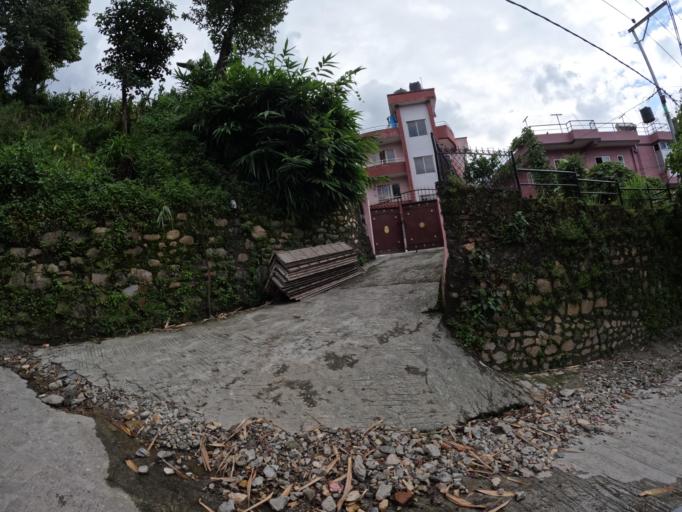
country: NP
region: Central Region
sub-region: Bagmati Zone
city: Kathmandu
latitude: 27.7402
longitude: 85.3182
